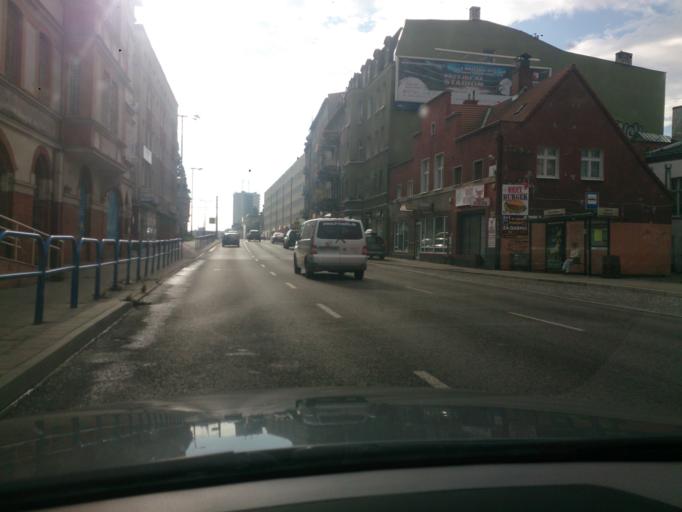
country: PL
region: Pomeranian Voivodeship
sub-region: Gdansk
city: Gdansk
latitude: 54.3817
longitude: 18.5991
